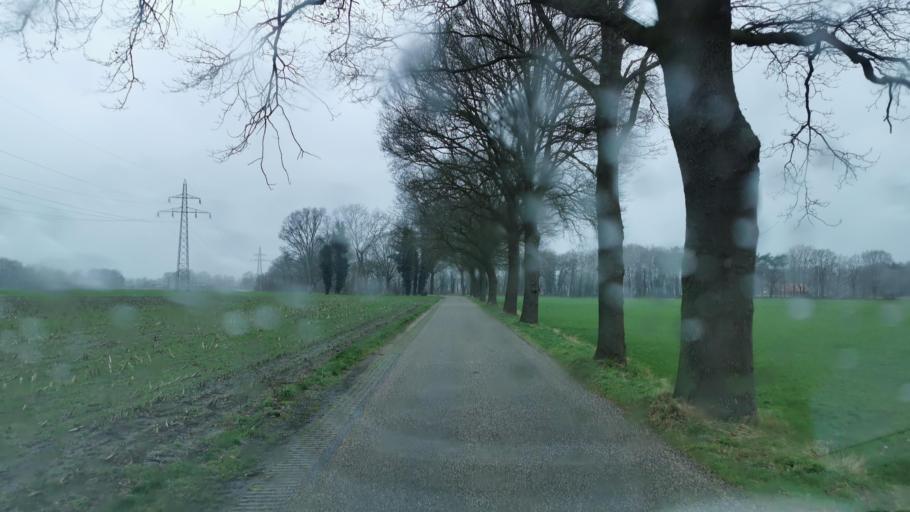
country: NL
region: Overijssel
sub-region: Gemeente Oldenzaal
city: Oldenzaal
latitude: 52.2969
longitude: 6.8746
